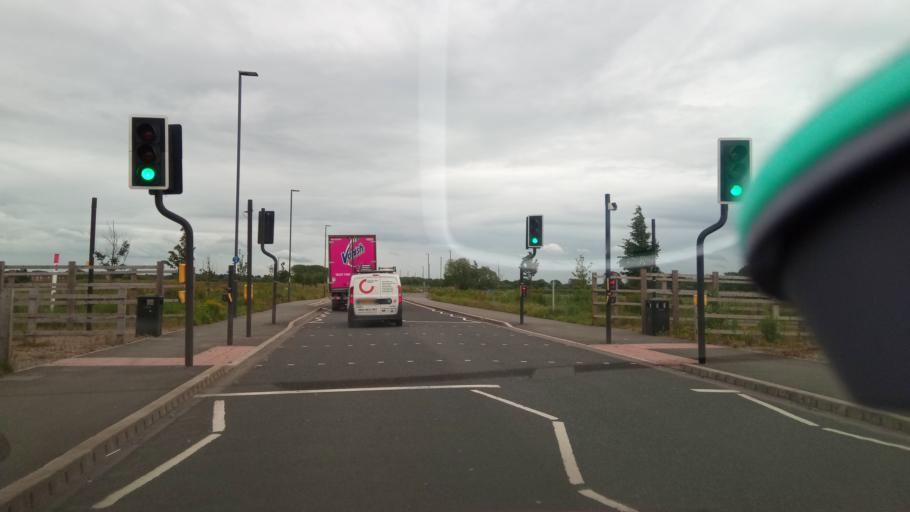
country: GB
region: England
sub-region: Derby
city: Derby
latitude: 52.8754
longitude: -1.4645
